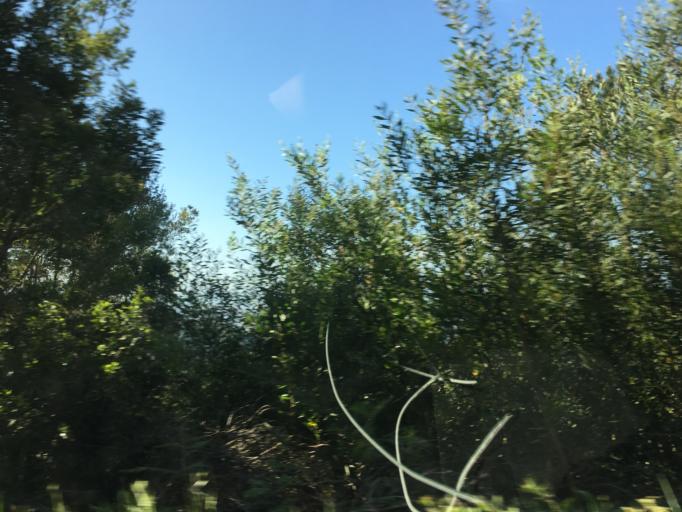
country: PT
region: Lisbon
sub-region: Sintra
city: Colares
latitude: 38.7696
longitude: -9.4452
